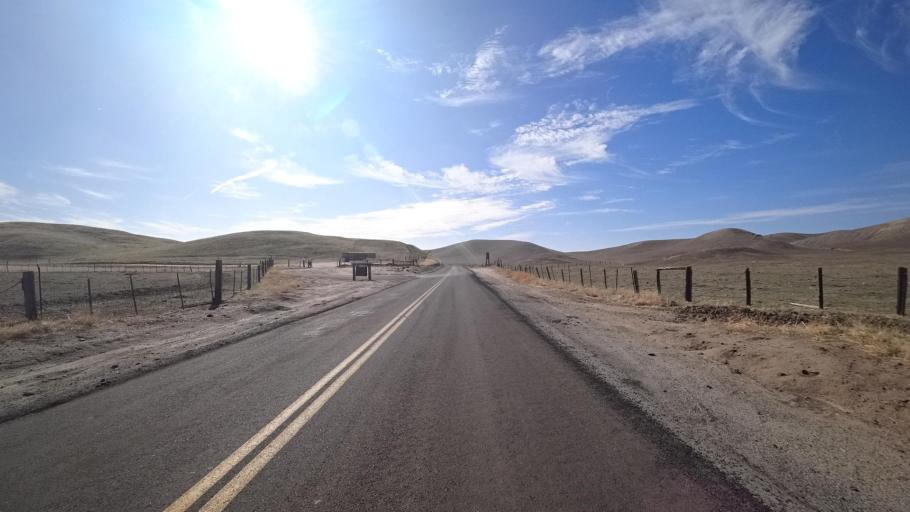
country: US
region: California
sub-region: Tulare County
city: Richgrove
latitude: 35.6465
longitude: -118.9400
